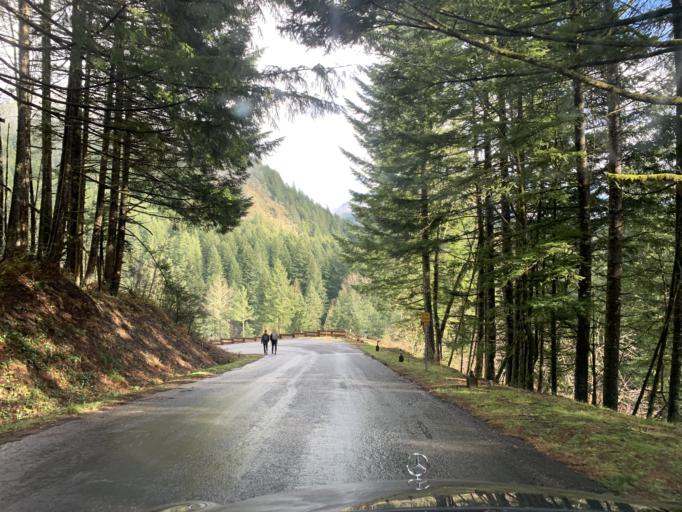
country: US
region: Washington
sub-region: Skamania County
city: Carson
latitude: 45.7270
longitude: -121.7977
